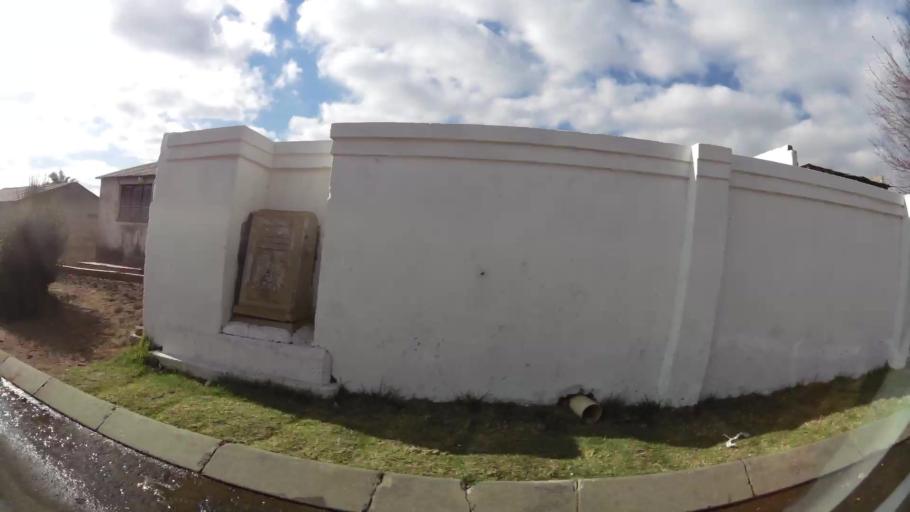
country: ZA
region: Gauteng
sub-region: City of Johannesburg Metropolitan Municipality
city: Roodepoort
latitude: -26.2130
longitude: 27.9094
